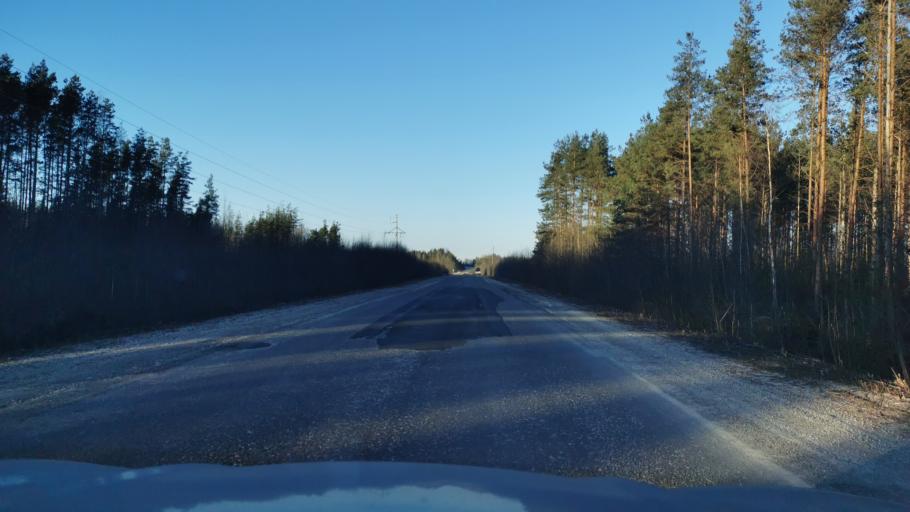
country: EE
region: Ida-Virumaa
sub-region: Puessi linn
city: Pussi
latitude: 59.3386
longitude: 27.0889
